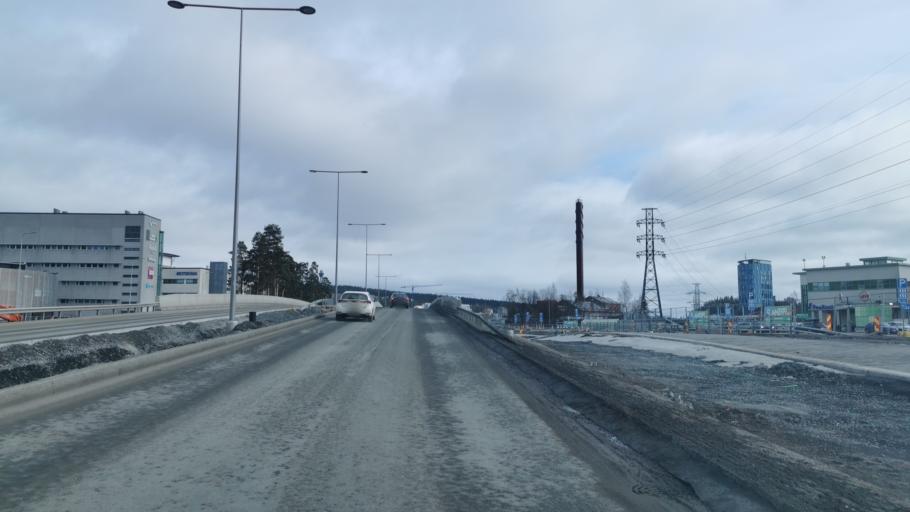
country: FI
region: Northern Savo
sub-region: Kuopio
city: Kuopio
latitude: 62.8878
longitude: 27.6303
